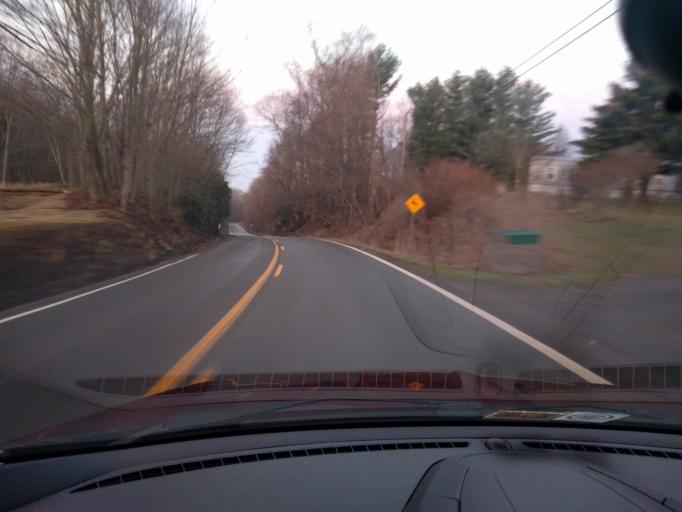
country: US
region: West Virginia
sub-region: Greenbrier County
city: Rainelle
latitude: 38.0119
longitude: -80.8838
